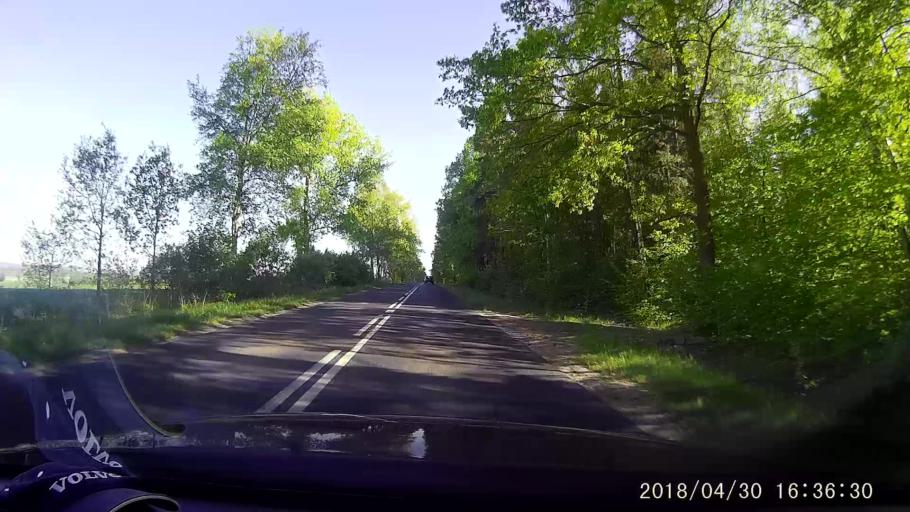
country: PL
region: Lower Silesian Voivodeship
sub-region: Powiat zgorzelecki
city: Sulikow
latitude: 51.0745
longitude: 15.0292
